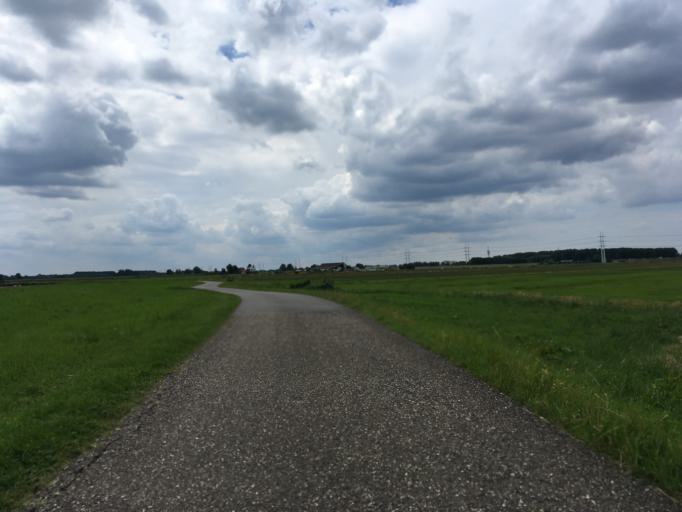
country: NL
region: North Holland
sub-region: Gemeente Velsen
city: Velsen-Zuid
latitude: 52.4105
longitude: 4.7204
